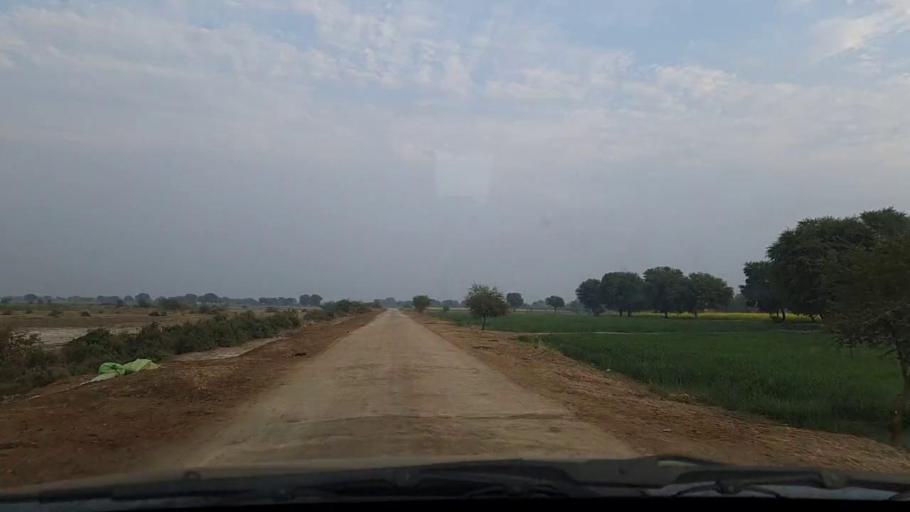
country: PK
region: Sindh
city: Pithoro
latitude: 25.5954
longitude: 69.4659
